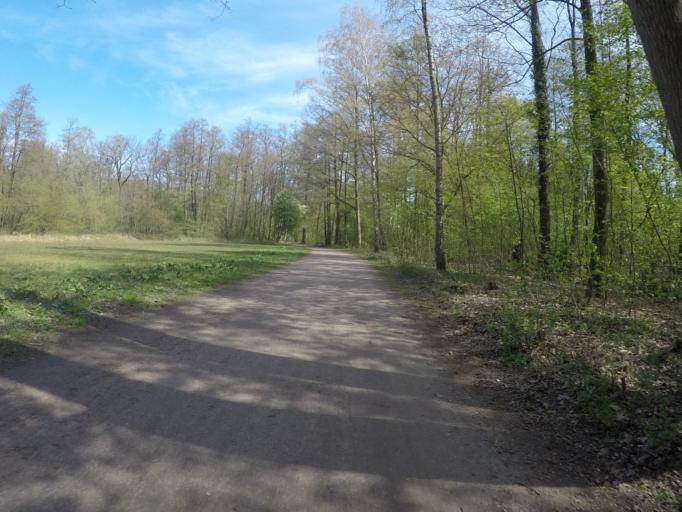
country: DE
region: Hamburg
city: Hummelsbuettel
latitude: 53.6349
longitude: 10.0472
